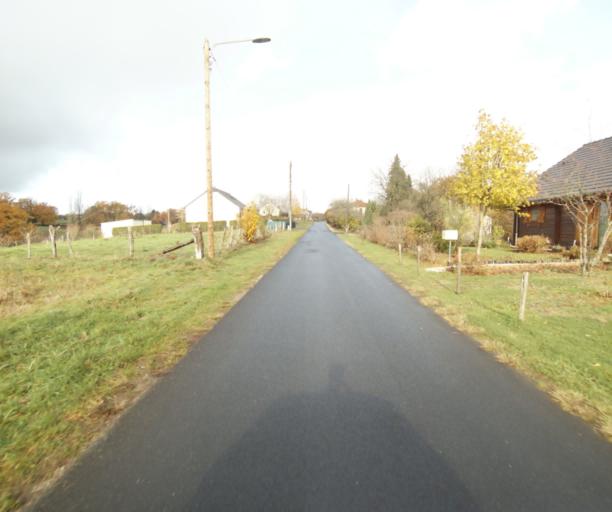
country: FR
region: Limousin
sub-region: Departement de la Correze
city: Saint-Mexant
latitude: 45.2375
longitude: 1.6340
